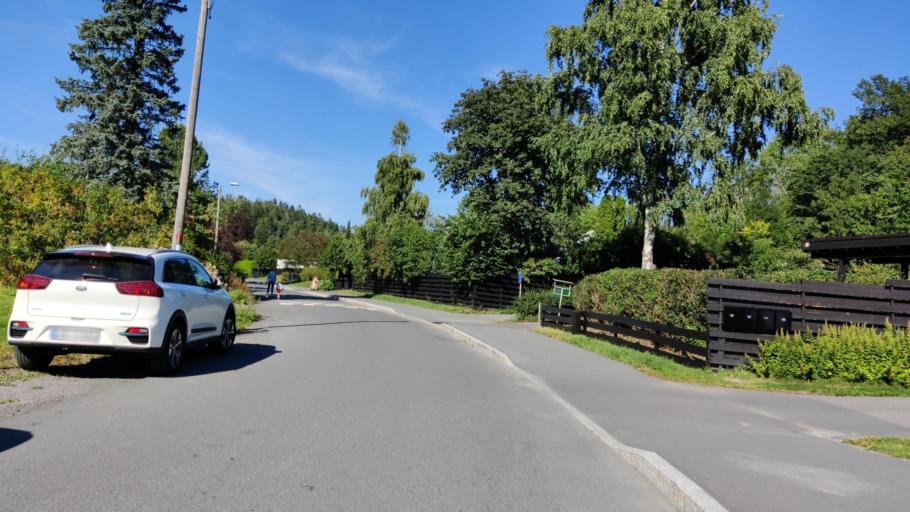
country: NO
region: Akershus
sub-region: Baerum
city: Lysaker
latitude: 59.9293
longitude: 10.6027
